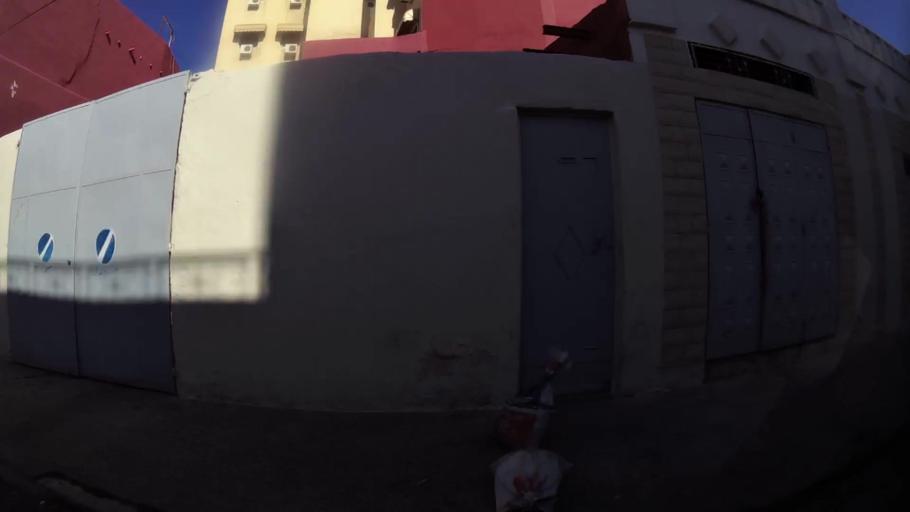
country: MA
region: Oriental
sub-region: Oujda-Angad
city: Oujda
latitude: 34.6810
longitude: -1.9210
